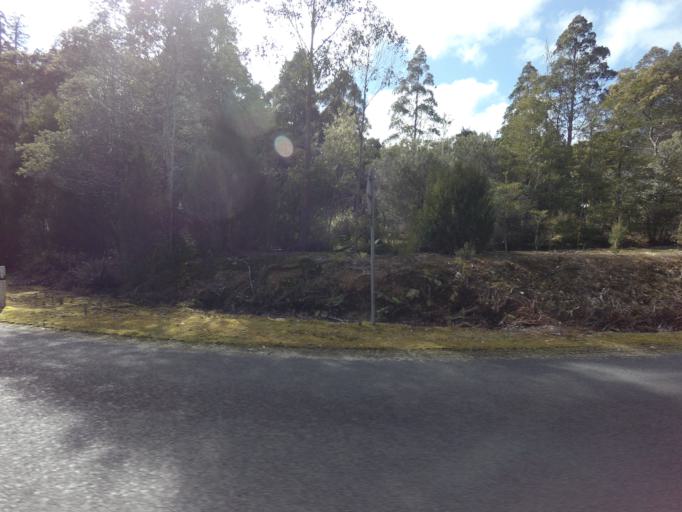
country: AU
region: Tasmania
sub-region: Huon Valley
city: Geeveston
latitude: -42.8194
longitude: 146.3315
